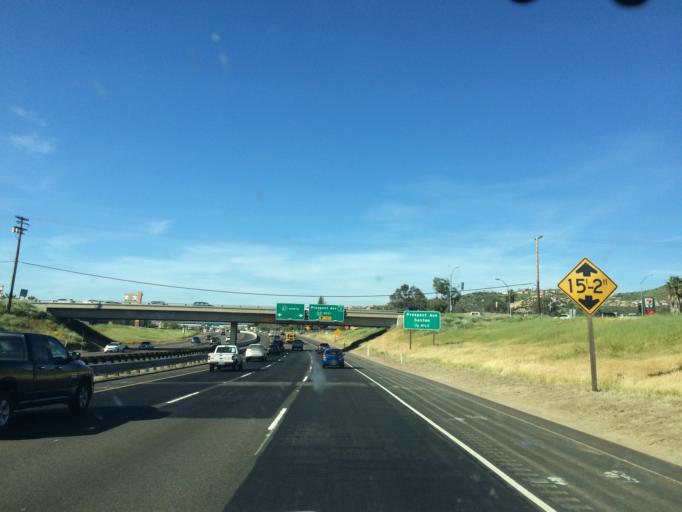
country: US
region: California
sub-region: San Diego County
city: El Cajon
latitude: 32.8169
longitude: -116.9607
